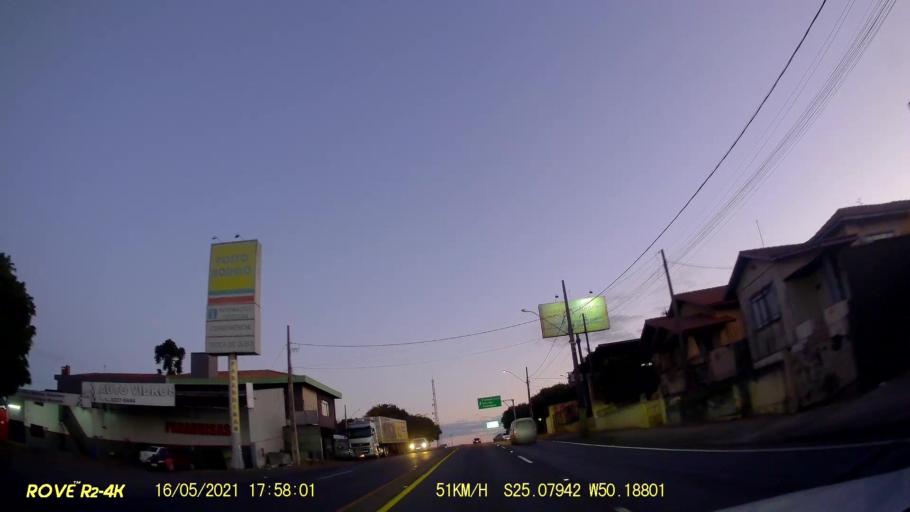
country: BR
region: Parana
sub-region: Ponta Grossa
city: Ponta Grossa
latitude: -25.0793
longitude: -50.1880
